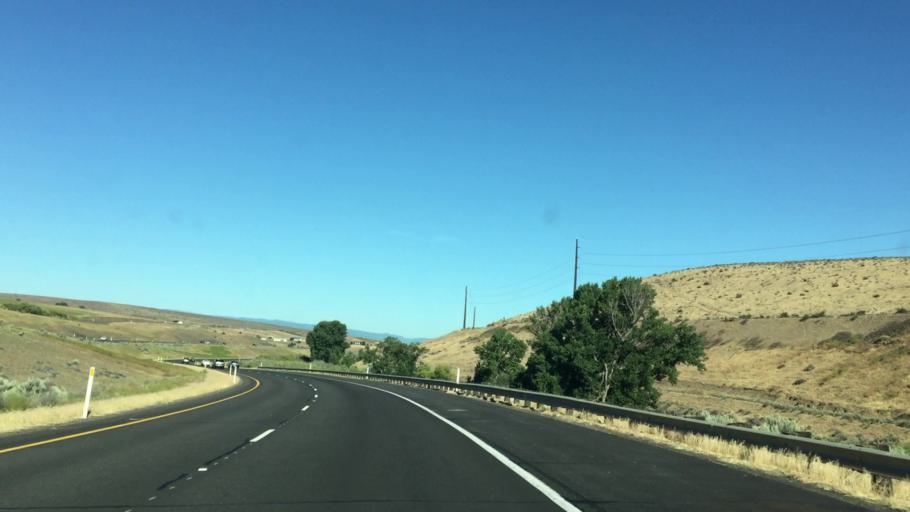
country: US
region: Washington
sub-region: Kittitas County
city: Kittitas
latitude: 46.9585
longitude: -120.3126
